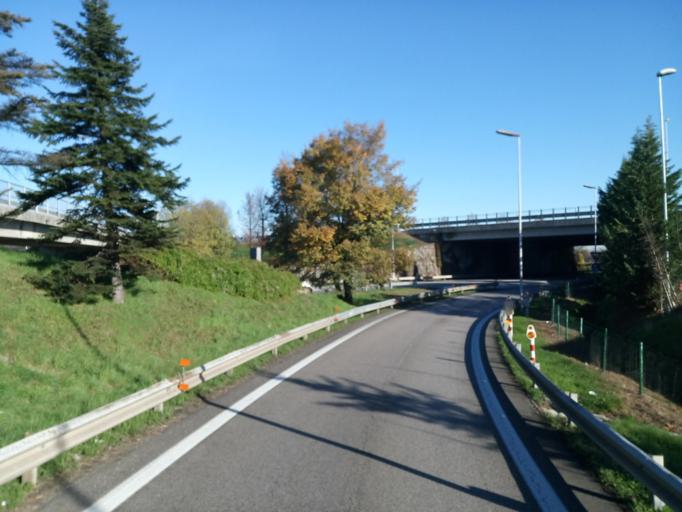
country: IT
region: Veneto
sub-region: Provincia di Vicenza
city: Lisiera
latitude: 45.5802
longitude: 11.5991
